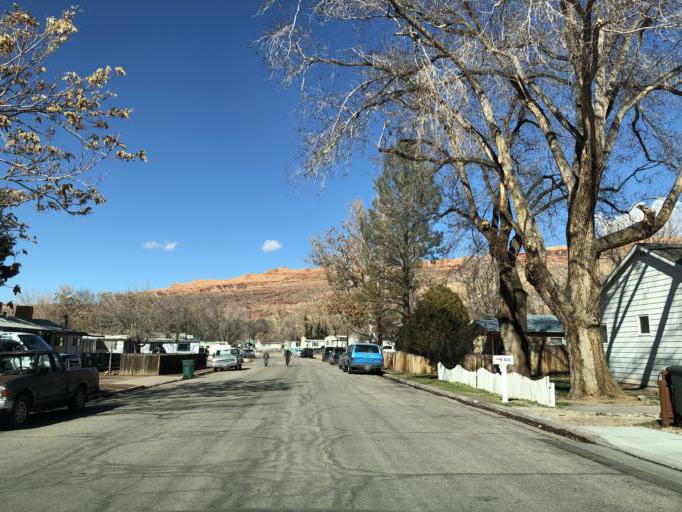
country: US
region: Utah
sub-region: Grand County
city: Moab
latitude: 38.5796
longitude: -109.5569
